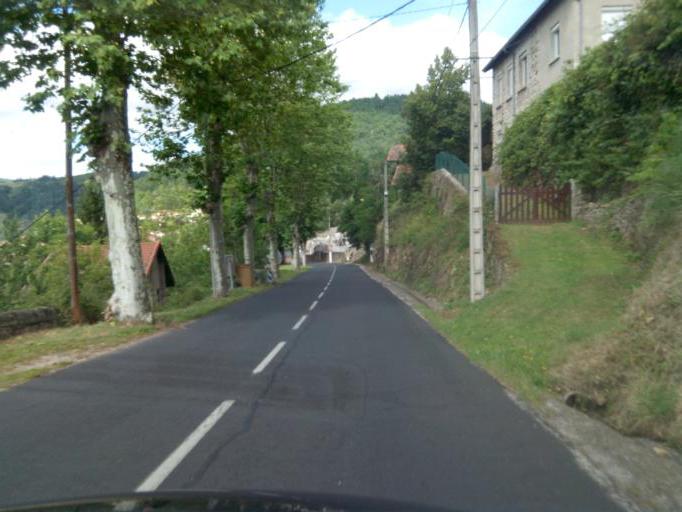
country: FR
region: Auvergne
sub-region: Departement de la Haute-Loire
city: Vorey
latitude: 45.1882
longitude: 3.9156
